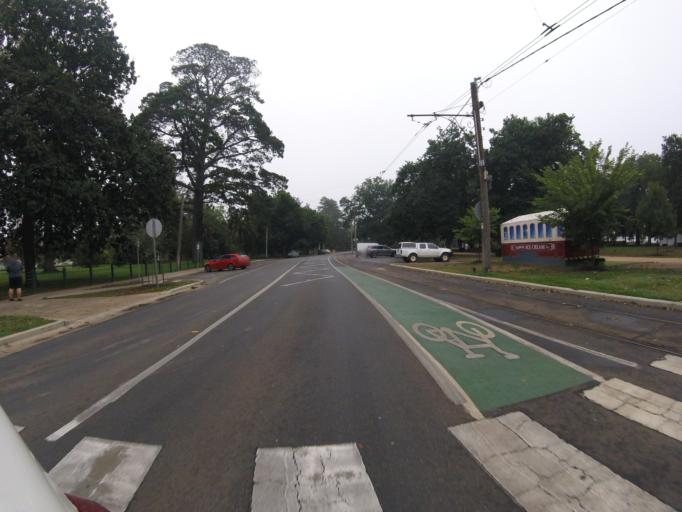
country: AU
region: Victoria
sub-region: Ballarat North
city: Newington
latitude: -37.5507
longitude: 143.8221
